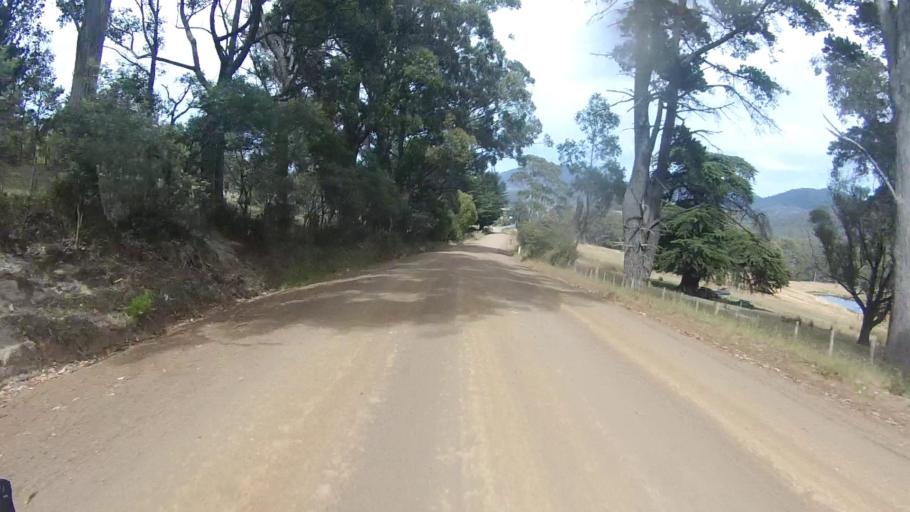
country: AU
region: Tasmania
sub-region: Sorell
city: Sorell
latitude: -42.7769
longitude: 147.8198
